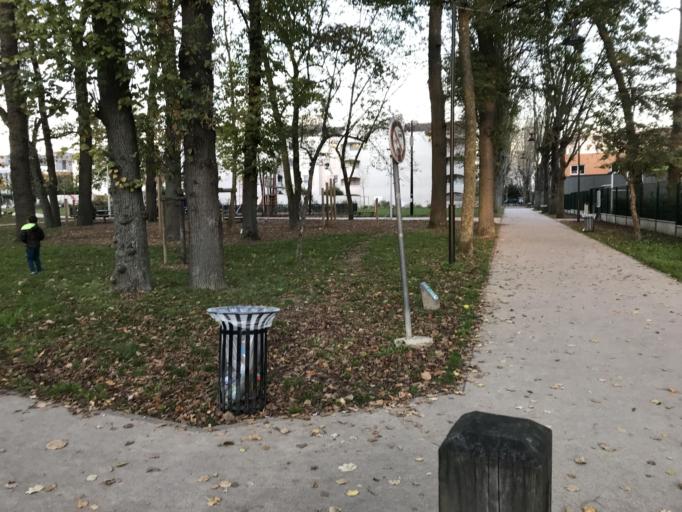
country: FR
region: Ile-de-France
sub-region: Departement de l'Essonne
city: Athis-Mons
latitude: 48.7077
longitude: 2.3829
